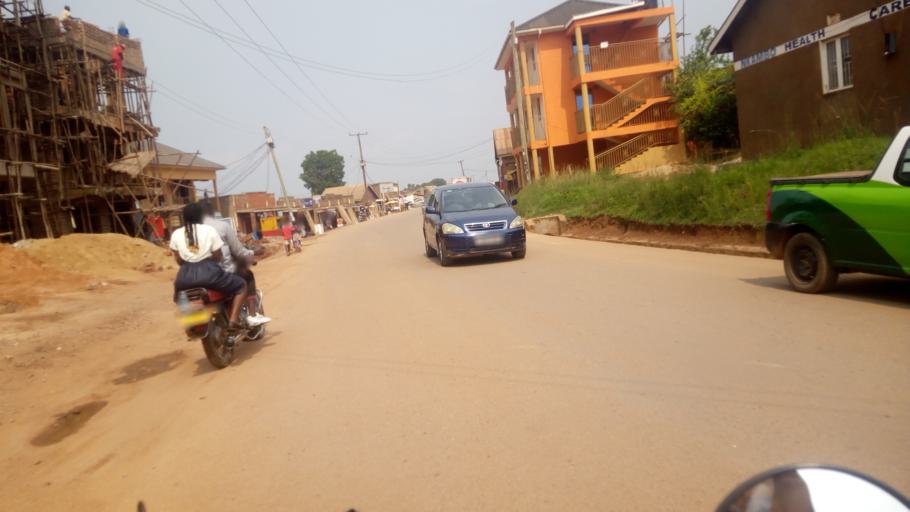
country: UG
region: Central Region
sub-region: Wakiso District
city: Kireka
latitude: 0.3187
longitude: 32.6488
